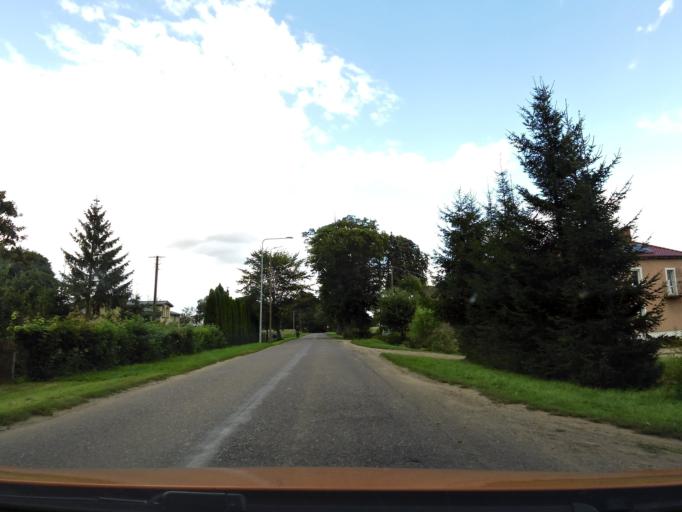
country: PL
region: West Pomeranian Voivodeship
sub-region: Powiat kolobrzeski
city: Ryman
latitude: 54.0179
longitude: 15.5186
